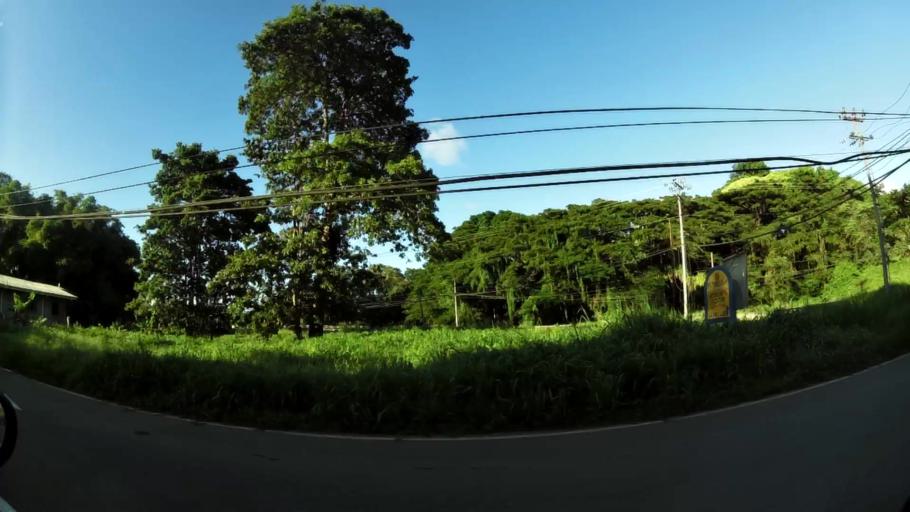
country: TT
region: Tobago
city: Scarborough
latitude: 11.2156
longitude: -60.7715
